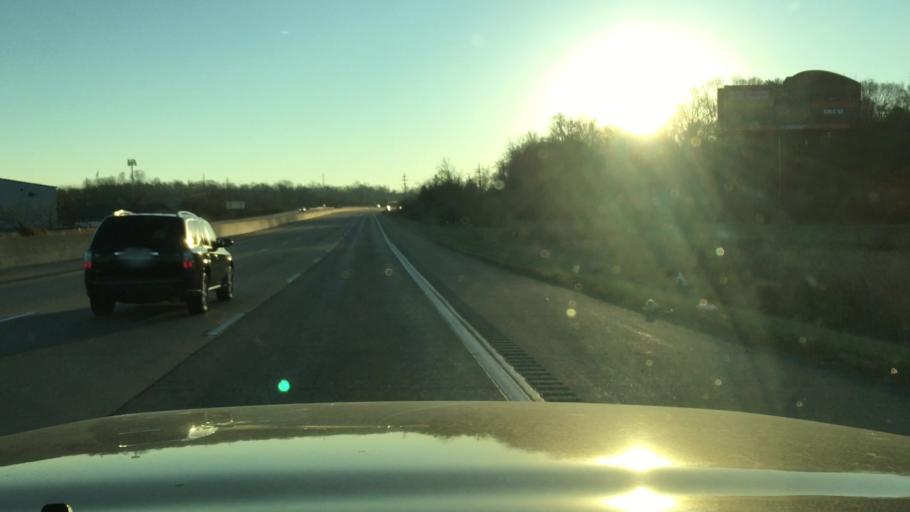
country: US
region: Missouri
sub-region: Saint Charles County
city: Saint Charles
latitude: 38.8200
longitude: -90.5033
